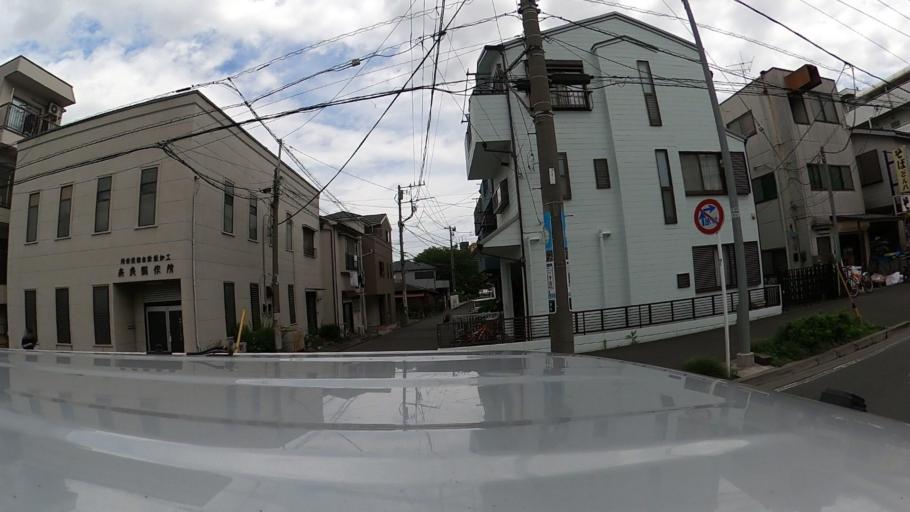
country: JP
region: Kanagawa
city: Yokohama
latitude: 35.4933
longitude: 139.6699
